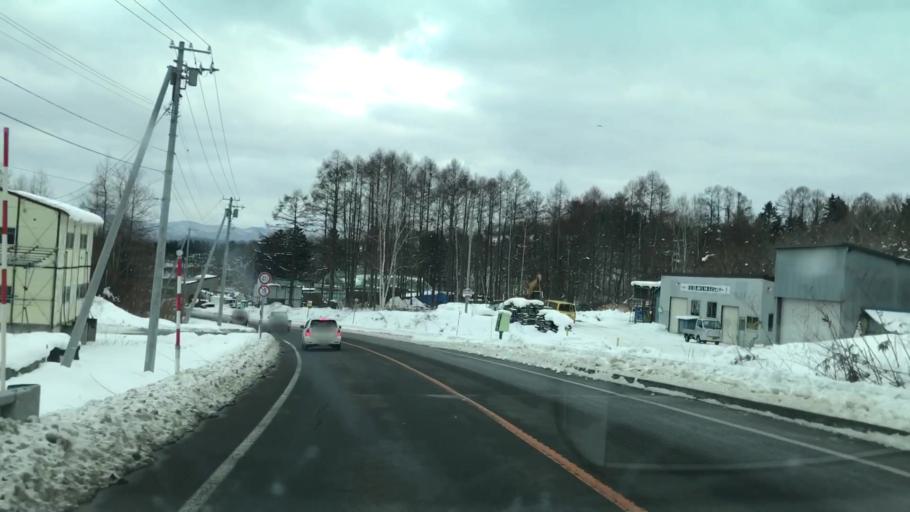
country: JP
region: Hokkaido
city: Yoichi
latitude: 43.2121
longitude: 140.7494
